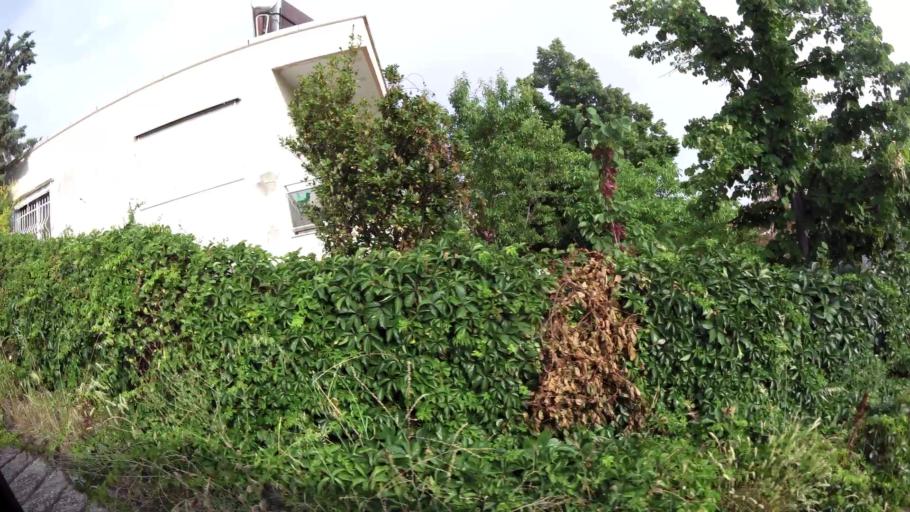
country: GR
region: Central Macedonia
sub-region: Nomos Thessalonikis
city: Oraiokastro
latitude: 40.7249
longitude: 22.9109
